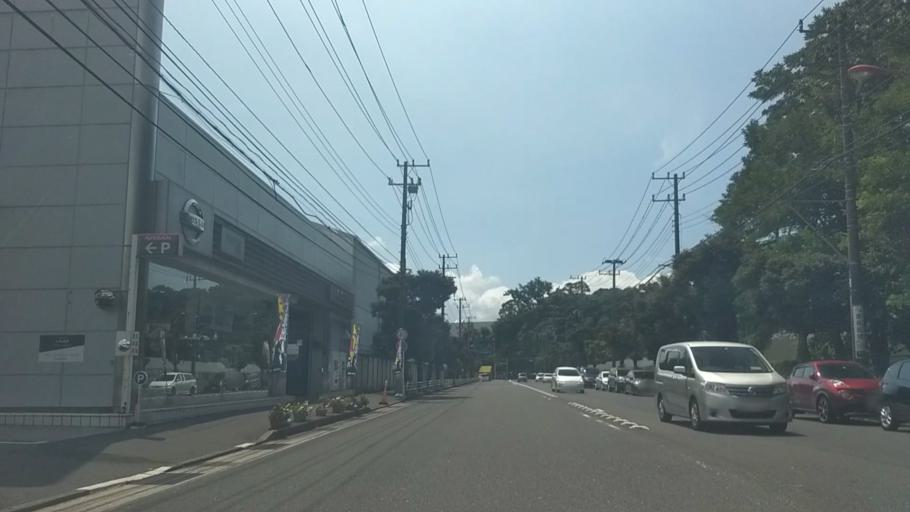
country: JP
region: Kanagawa
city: Yokosuka
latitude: 35.3188
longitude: 139.6364
